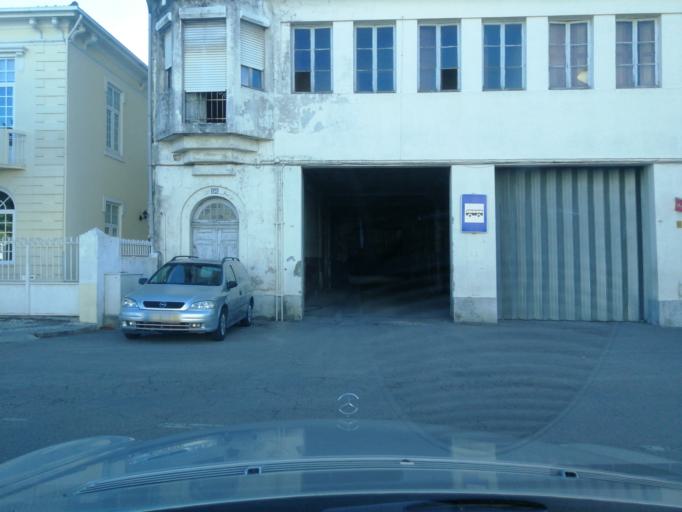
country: PT
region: Aveiro
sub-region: Agueda
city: Agueda
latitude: 40.5752
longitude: -8.4482
